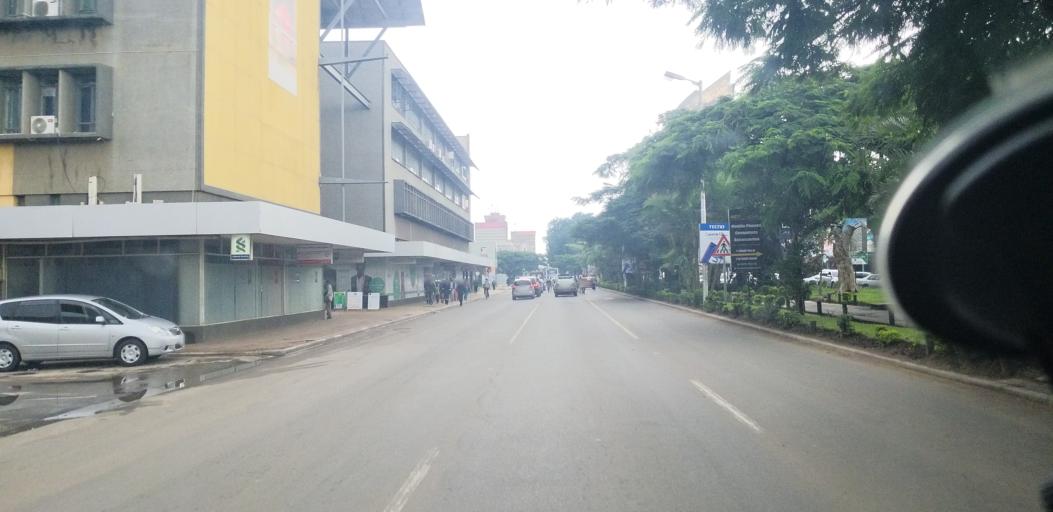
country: ZM
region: Lusaka
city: Lusaka
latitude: -15.4145
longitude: 28.2814
